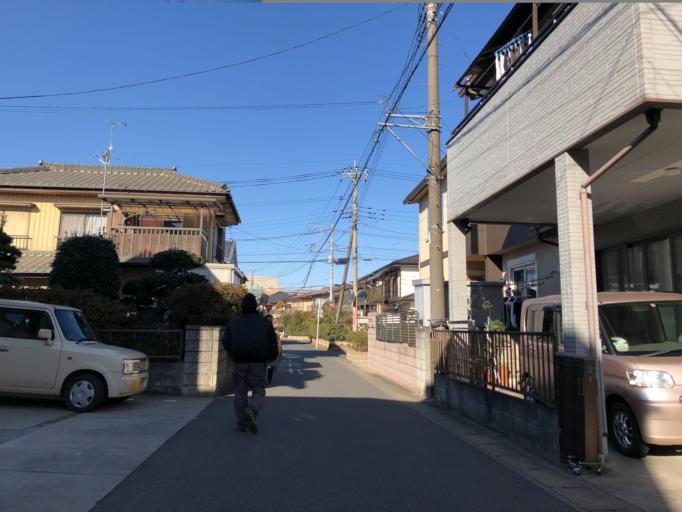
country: JP
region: Saitama
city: Sugito
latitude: 36.0263
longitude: 139.7178
